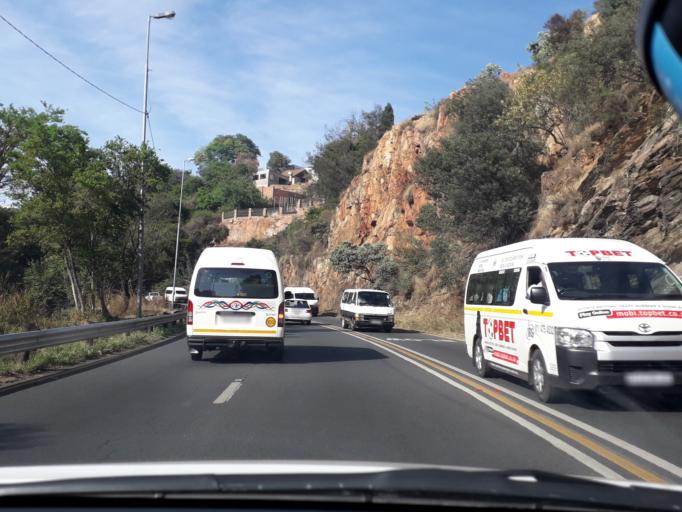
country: ZA
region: Gauteng
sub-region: City of Johannesburg Metropolitan Municipality
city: Roodepoort
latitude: -26.1317
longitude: 27.8933
